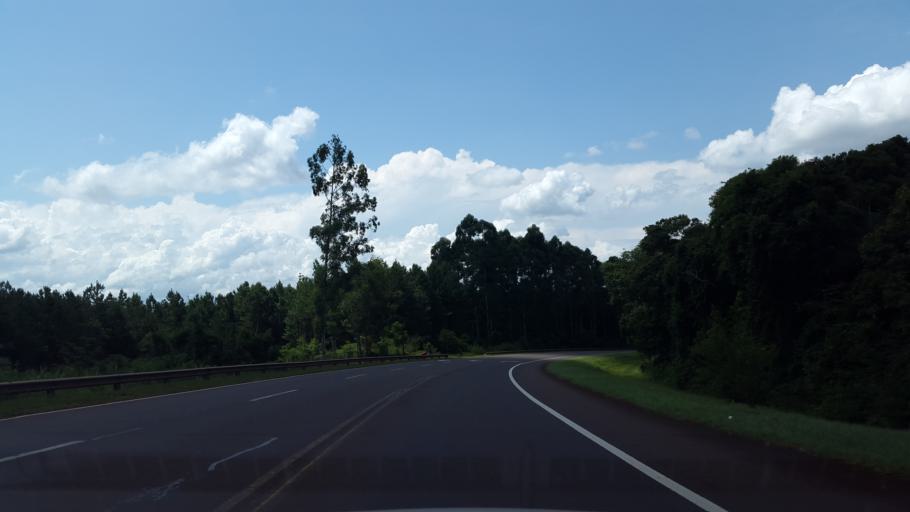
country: AR
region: Misiones
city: El Alcazar
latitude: -26.6938
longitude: -54.8320
